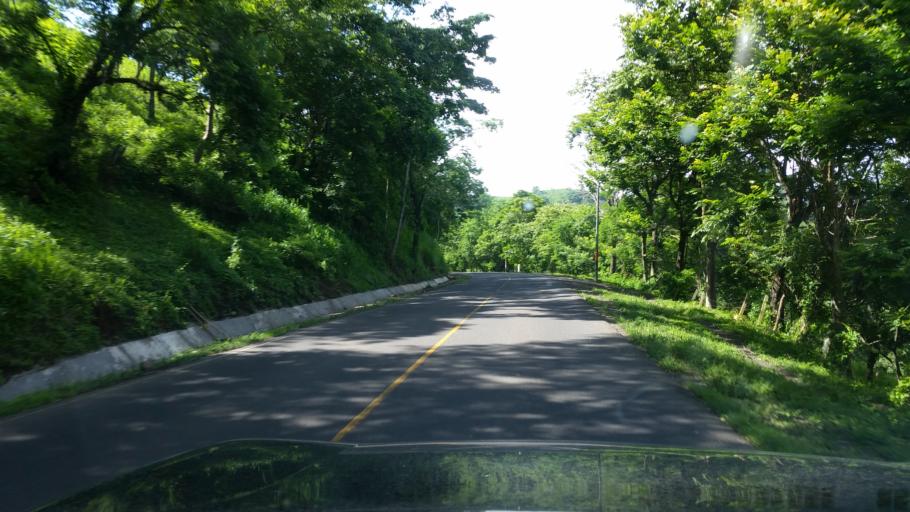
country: NI
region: Matagalpa
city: San Ramon
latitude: 13.0085
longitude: -85.7970
